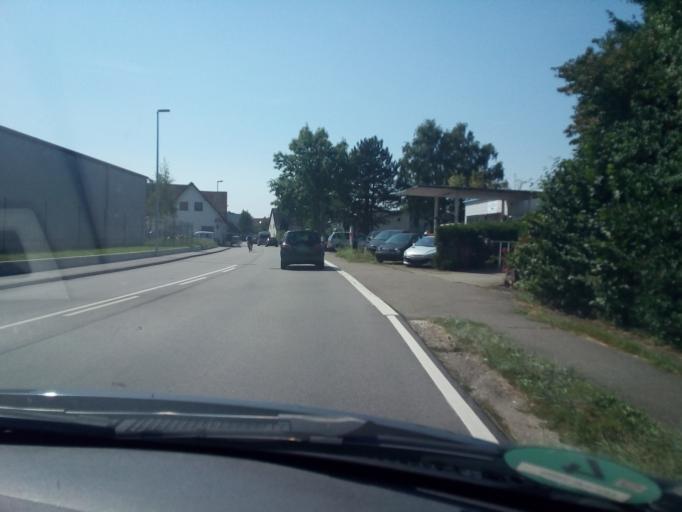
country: DE
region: Baden-Wuerttemberg
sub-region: Karlsruhe Region
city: Ottenhofen
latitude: 48.7287
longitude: 8.0917
